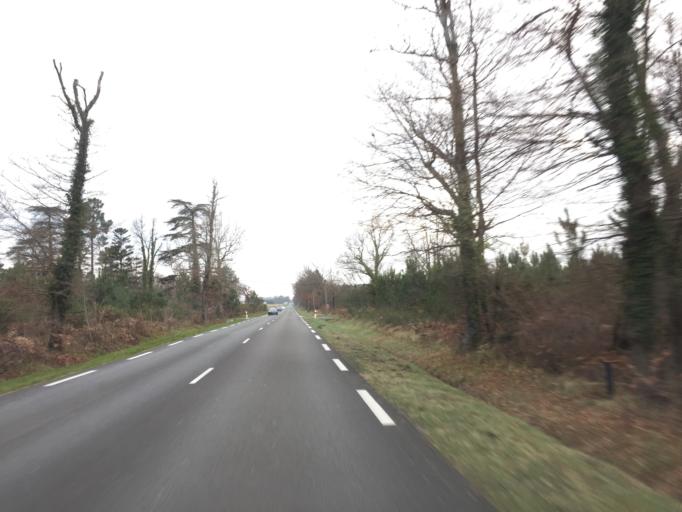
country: FR
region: Aquitaine
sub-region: Departement de la Gironde
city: Saint-Sauveur
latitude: 45.1941
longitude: -0.8539
